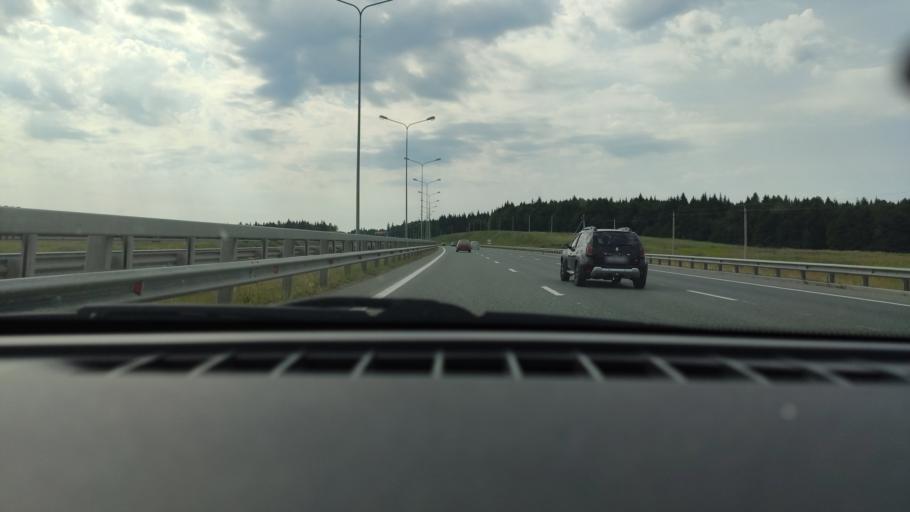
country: RU
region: Perm
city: Zvezdnyy
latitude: 57.7692
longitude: 56.3358
